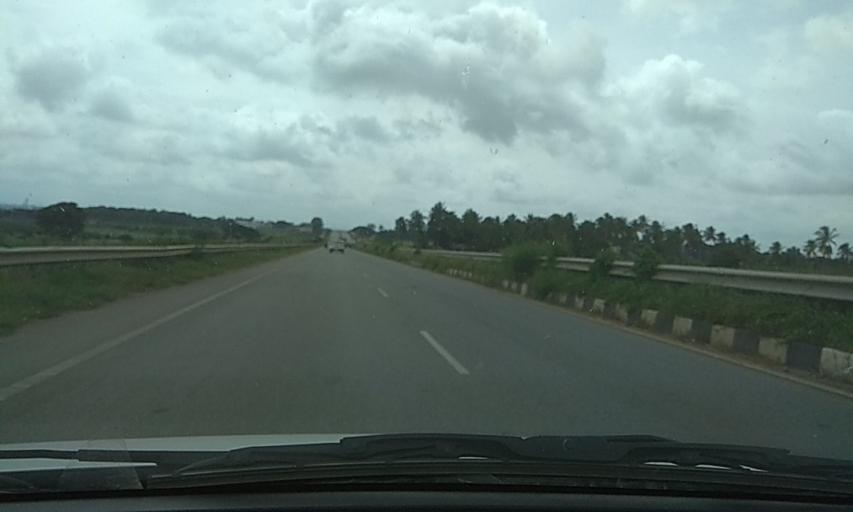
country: IN
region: Karnataka
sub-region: Davanagere
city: Harihar
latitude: 14.4584
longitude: 75.8605
